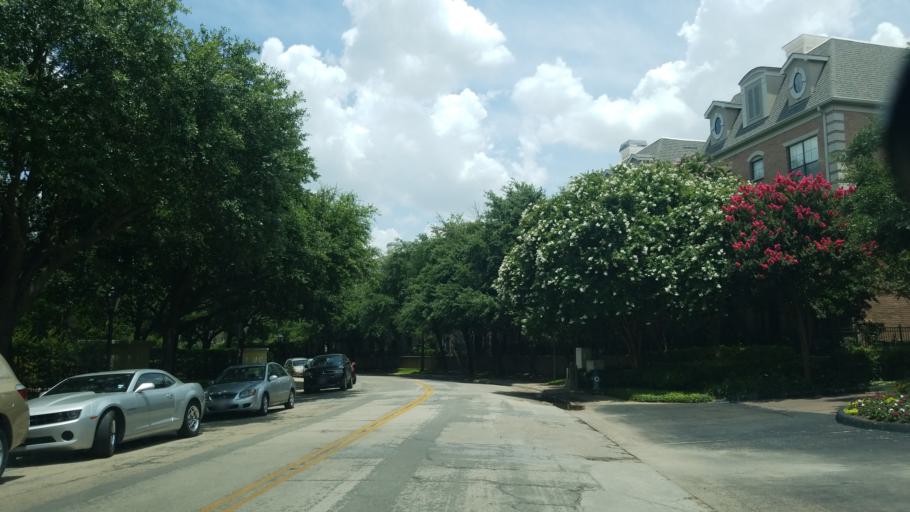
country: US
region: Texas
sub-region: Dallas County
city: University Park
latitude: 32.8664
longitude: -96.7919
